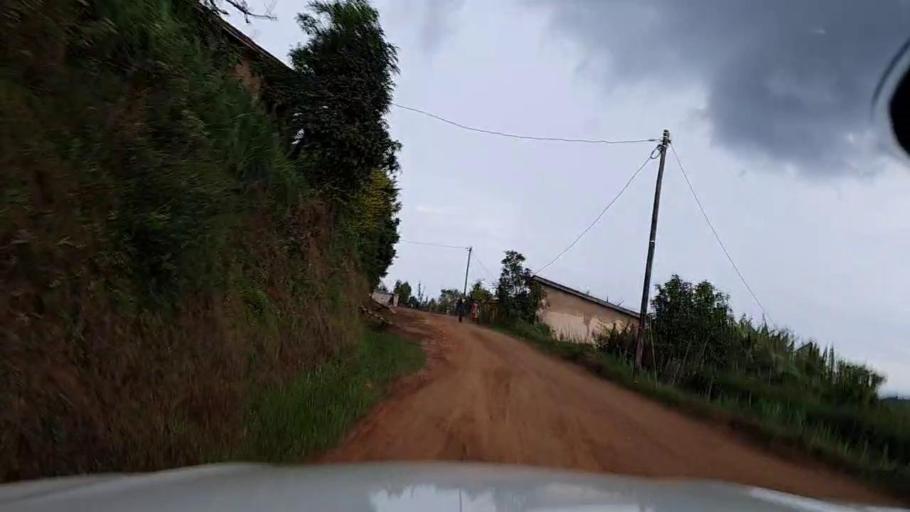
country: BI
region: Kayanza
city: Kayanza
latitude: -2.7883
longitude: 29.5288
